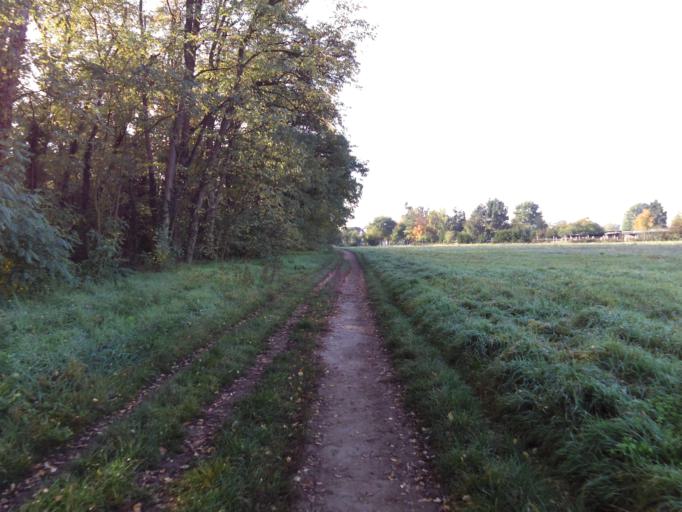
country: DE
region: Rheinland-Pfalz
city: Birkenheide
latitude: 49.4844
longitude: 8.2578
